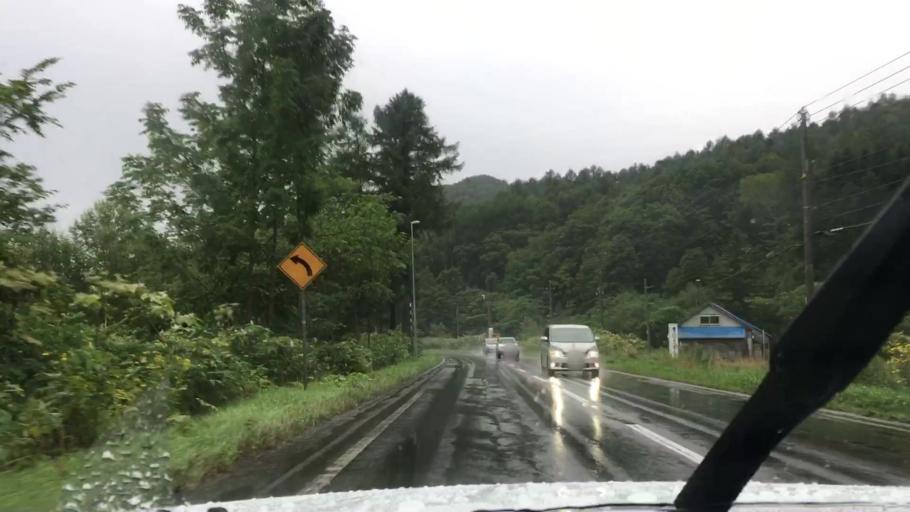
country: JP
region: Hokkaido
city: Niseko Town
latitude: 42.8243
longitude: 141.0040
